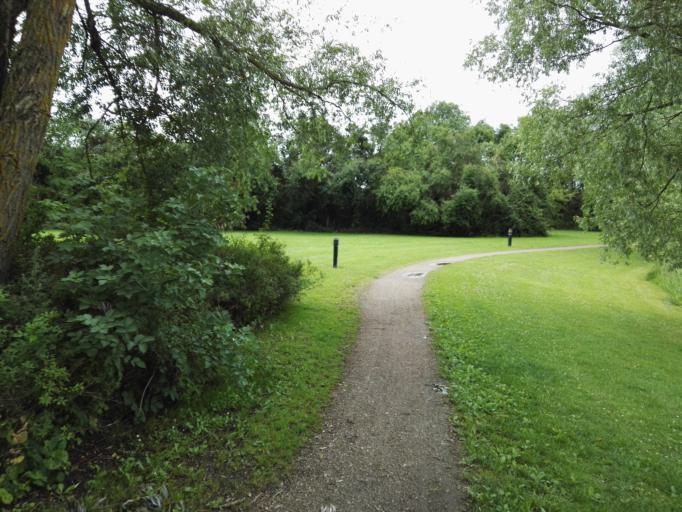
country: DK
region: Capital Region
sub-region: Egedal Kommune
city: Stenlose
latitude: 55.7725
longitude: 12.1742
